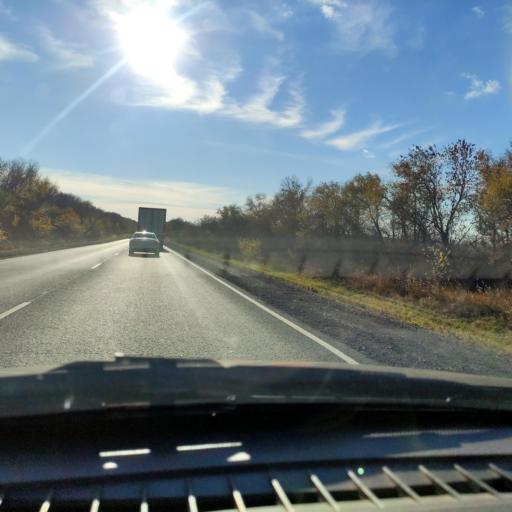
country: RU
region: Samara
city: Zhigulevsk
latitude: 53.2994
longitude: 49.3418
